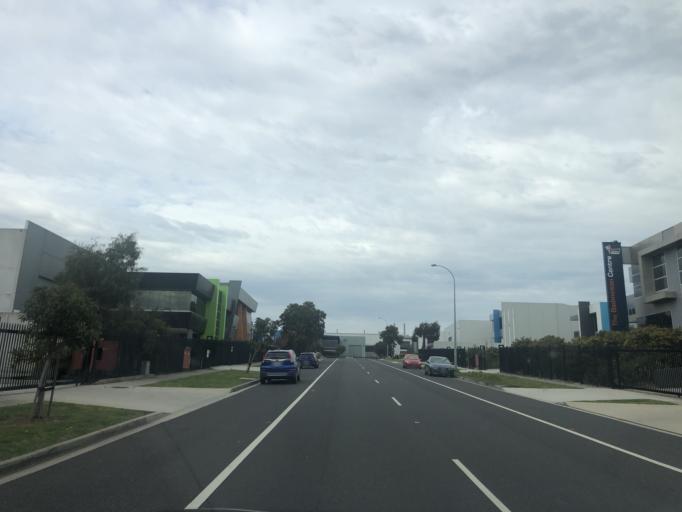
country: AU
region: Victoria
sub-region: Casey
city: Hallam
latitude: -38.0097
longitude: 145.2591
